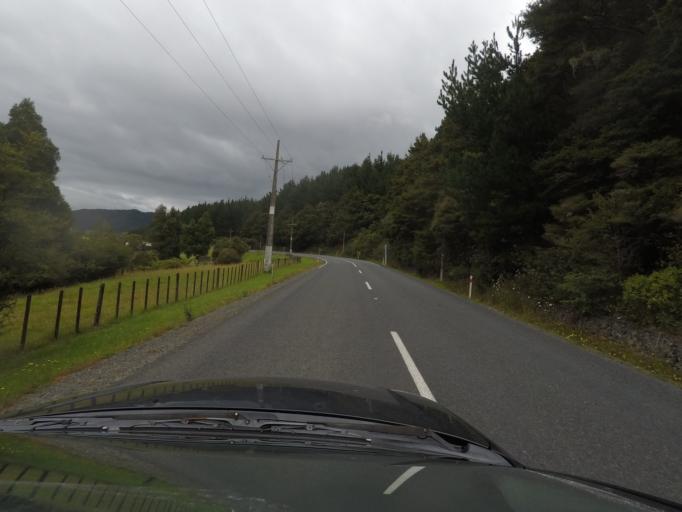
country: NZ
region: Auckland
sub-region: Auckland
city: Wellsford
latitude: -36.2866
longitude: 174.6130
